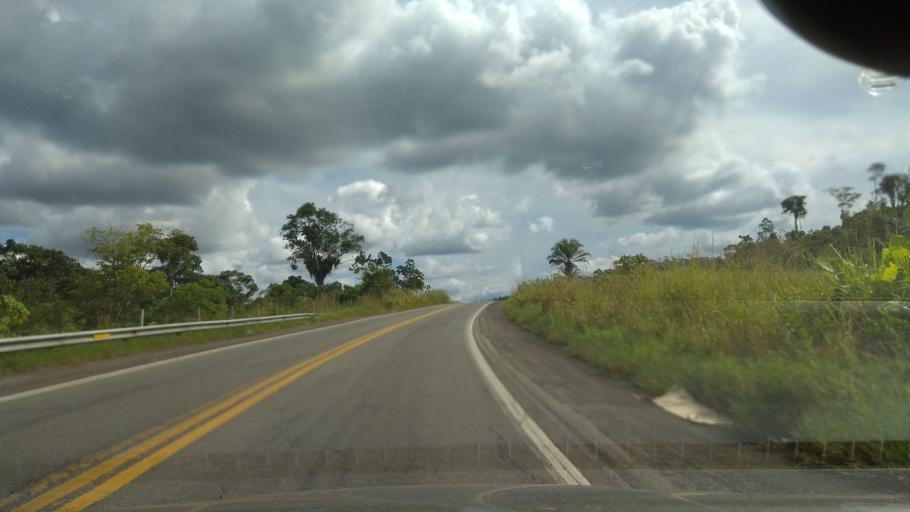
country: BR
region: Bahia
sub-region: Ubaitaba
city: Ubaitaba
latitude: -14.2517
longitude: -39.3680
